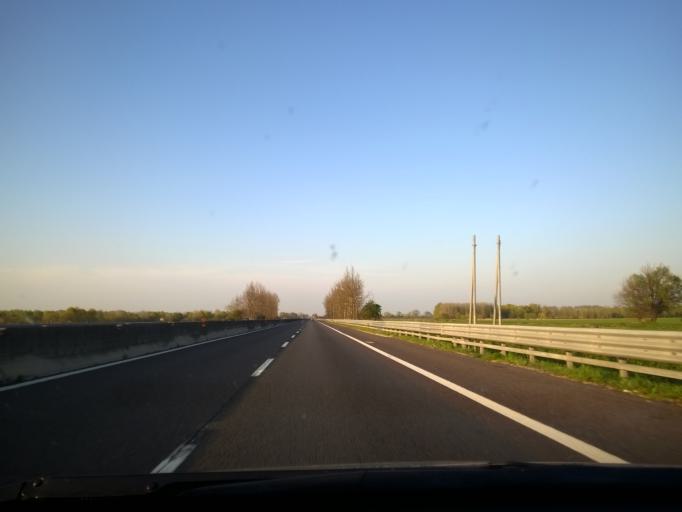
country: IT
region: Emilia-Romagna
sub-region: Provincia di Bologna
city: Altedo
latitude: 44.7037
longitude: 11.4926
